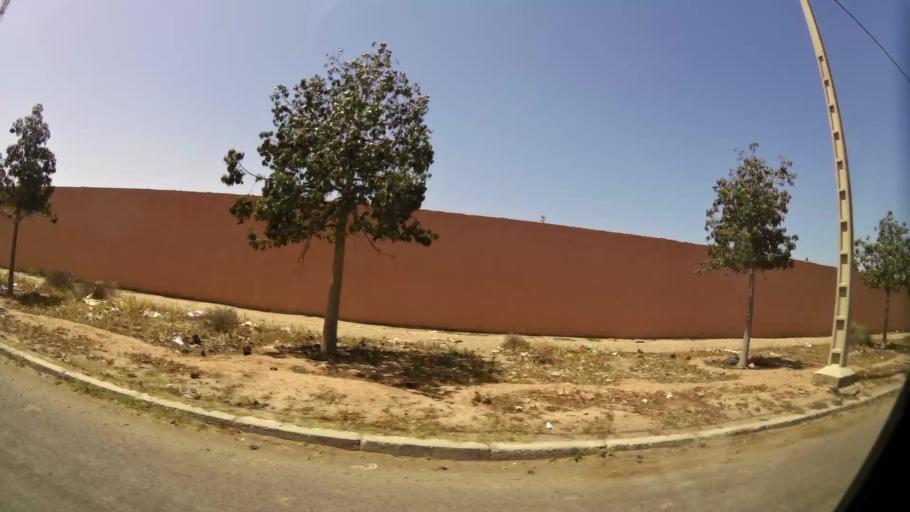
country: MA
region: Souss-Massa-Draa
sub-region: Inezgane-Ait Mellou
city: Inezgane
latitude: 30.3335
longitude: -9.4853
